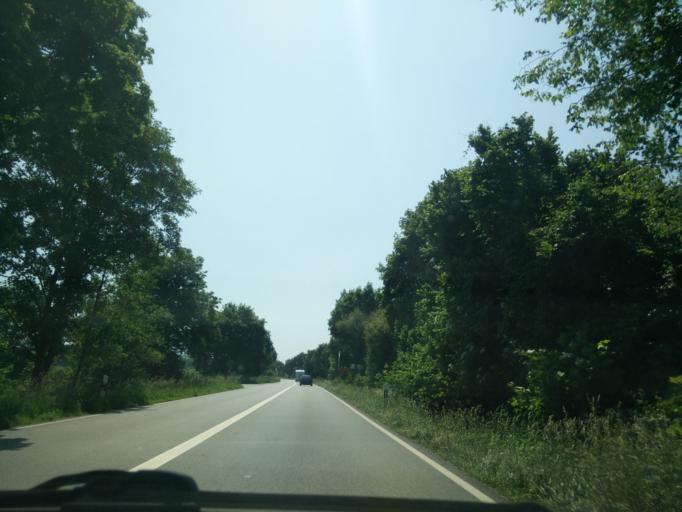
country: DE
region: Bavaria
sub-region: Upper Bavaria
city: Laufen
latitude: 47.9030
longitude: 12.9467
